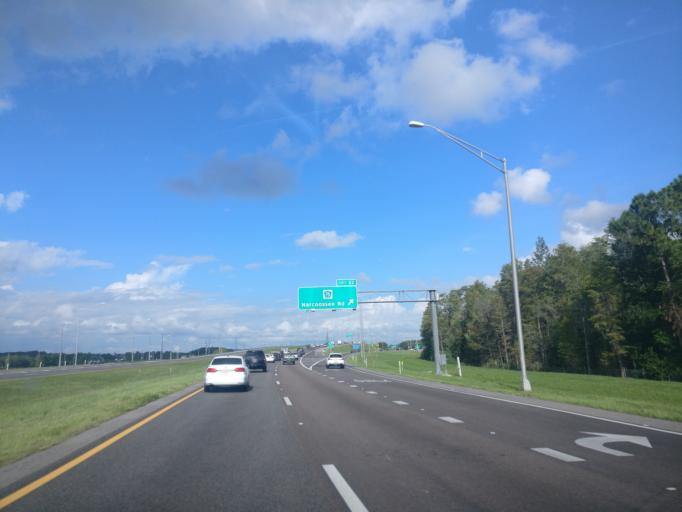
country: US
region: Florida
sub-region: Orange County
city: Meadow Woods
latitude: 28.3971
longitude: -81.2497
